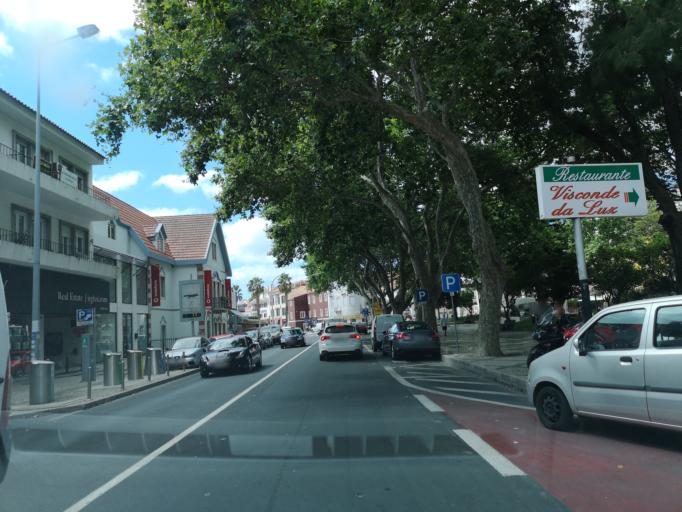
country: PT
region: Lisbon
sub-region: Cascais
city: Cascais
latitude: 38.6999
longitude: -9.4206
